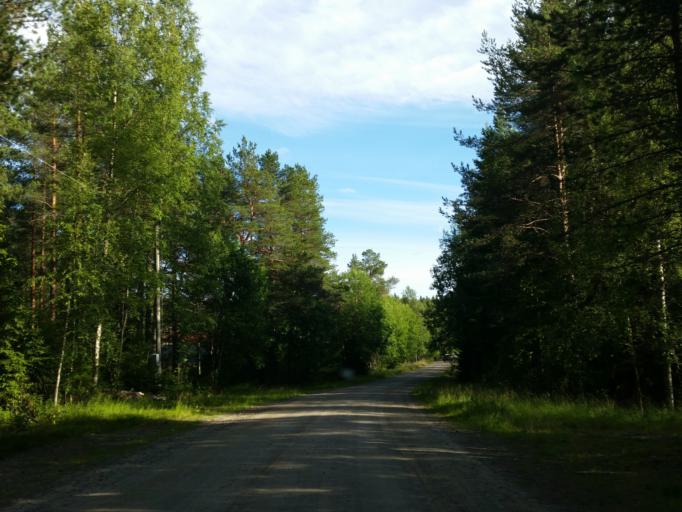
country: SE
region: Vaesterbotten
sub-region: Robertsfors Kommun
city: Robertsfors
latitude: 64.0394
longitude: 20.8503
